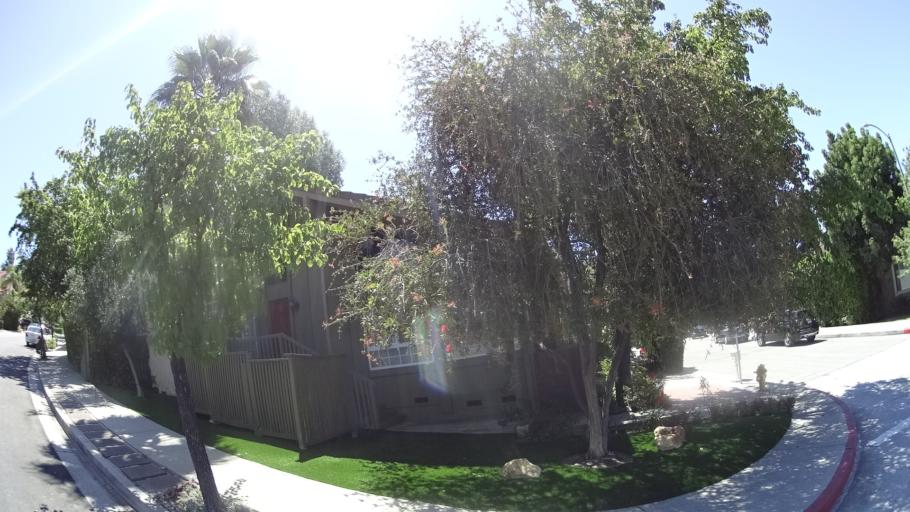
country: US
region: California
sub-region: Los Angeles County
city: Sherman Oaks
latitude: 34.1261
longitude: -118.4448
